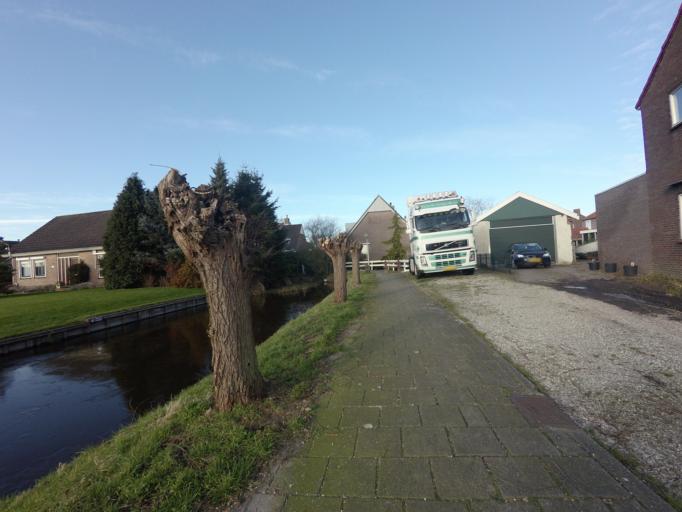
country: NL
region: Utrecht
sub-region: Gemeente Woerden
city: Woerden
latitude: 52.0766
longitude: 4.8181
